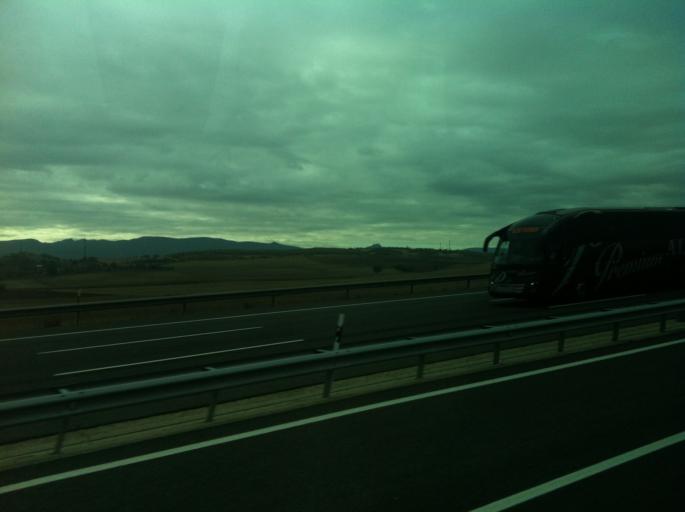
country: ES
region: Basque Country
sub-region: Provincia de Alava
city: Arminon
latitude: 42.7069
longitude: -2.8817
